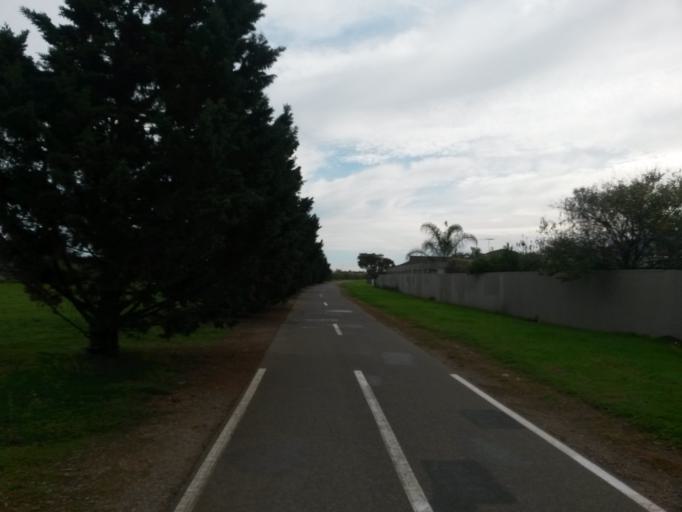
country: AU
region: South Australia
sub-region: Onkaparinga
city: Moana
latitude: -35.1953
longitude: 138.4860
